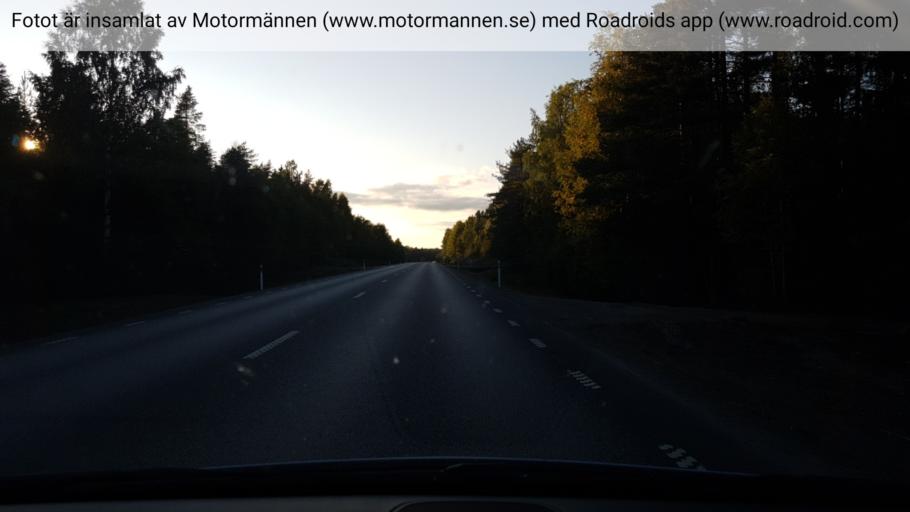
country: SE
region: Vaesterbotten
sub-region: Umea Kommun
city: Roback
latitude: 63.8519
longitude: 20.1108
